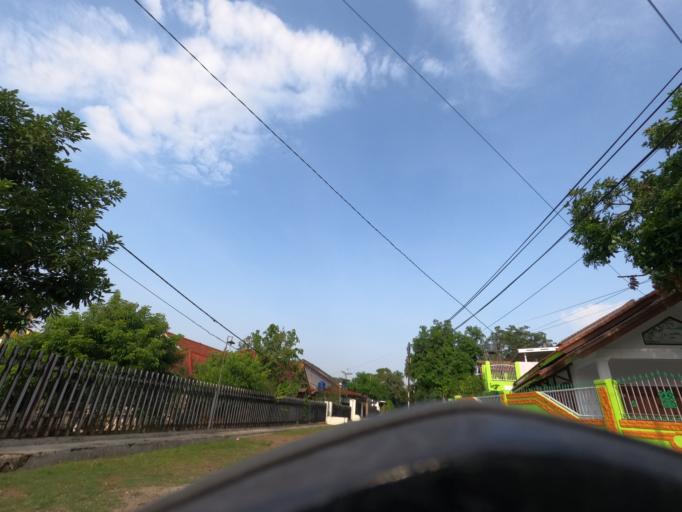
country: ID
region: West Java
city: Lembang
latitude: -6.5794
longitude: 107.7647
